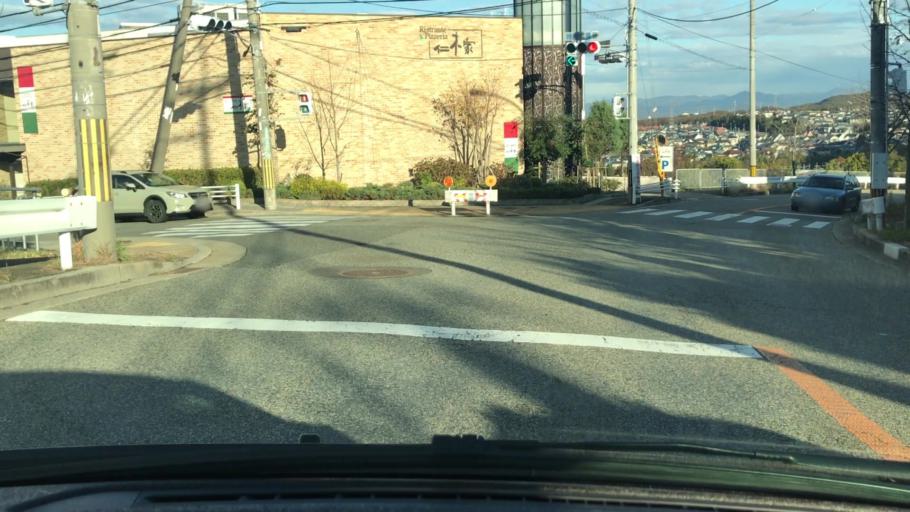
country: JP
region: Hyogo
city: Sandacho
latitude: 34.8228
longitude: 135.2505
